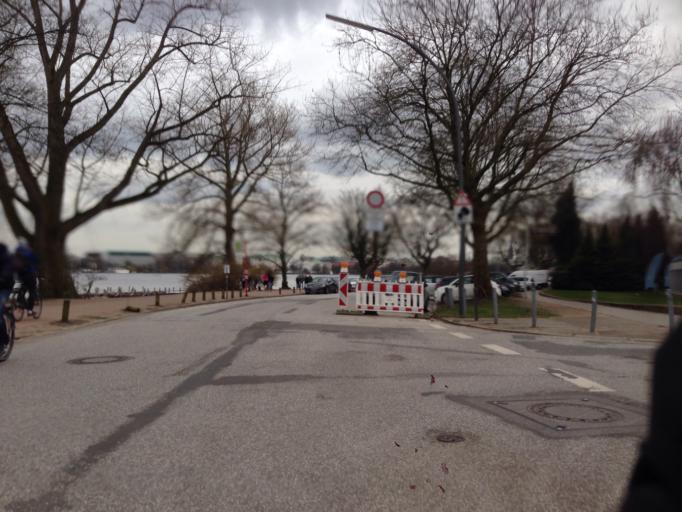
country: DE
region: Hamburg
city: Hamburg
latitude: 53.5674
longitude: 10.0012
